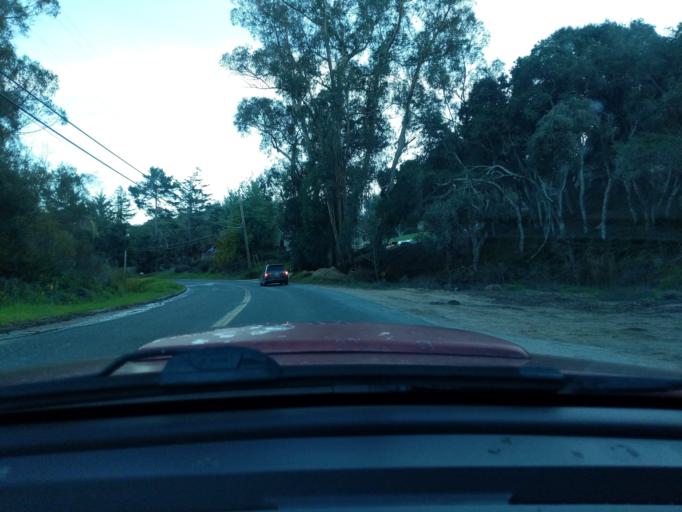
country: US
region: California
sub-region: San Benito County
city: Aromas
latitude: 36.8515
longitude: -121.6805
